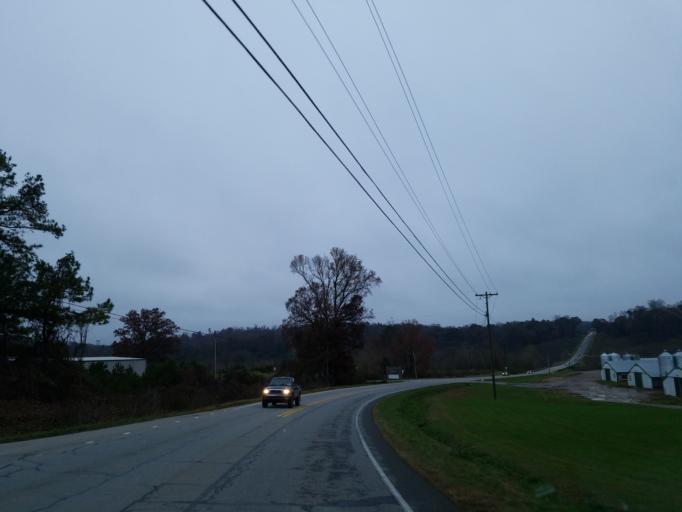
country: US
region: Georgia
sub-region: Pickens County
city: Nelson
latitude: 34.4002
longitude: -84.4322
